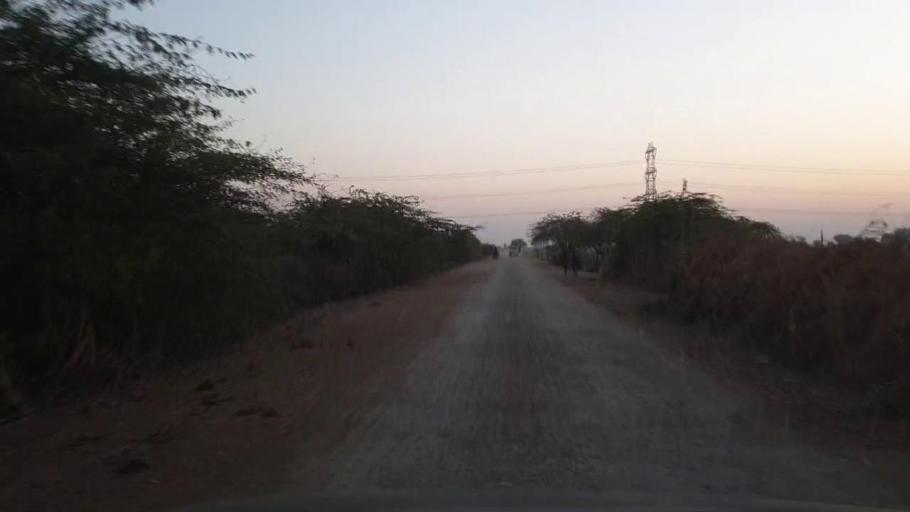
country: PK
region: Sindh
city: Digri
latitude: 25.1978
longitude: 69.1929
